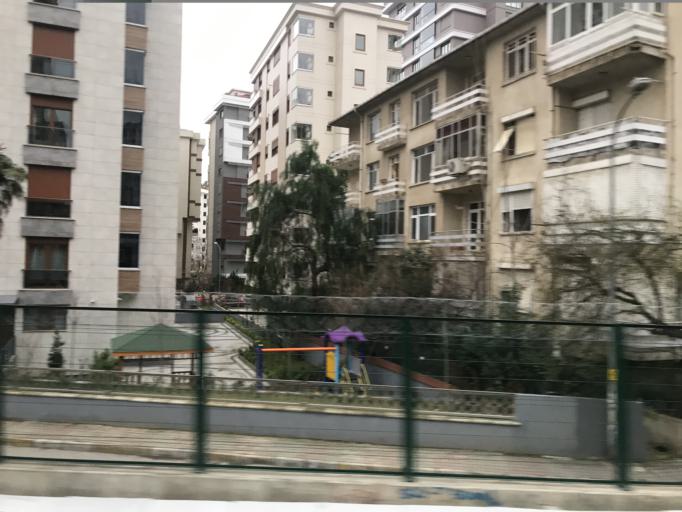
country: TR
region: Istanbul
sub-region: Atasehir
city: Atasehir
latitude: 40.9673
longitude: 29.0786
